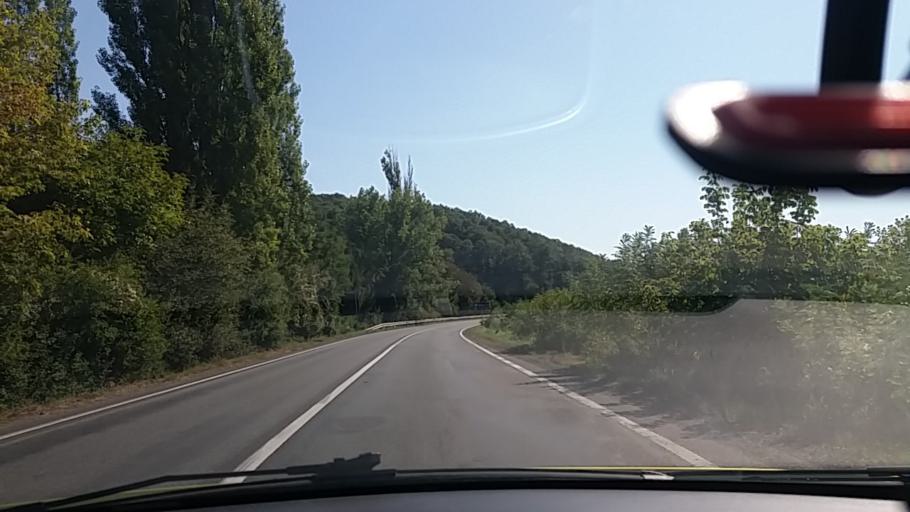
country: RO
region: Arad
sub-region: Comuna Ususau
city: Ususau
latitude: 46.0927
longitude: 21.7923
